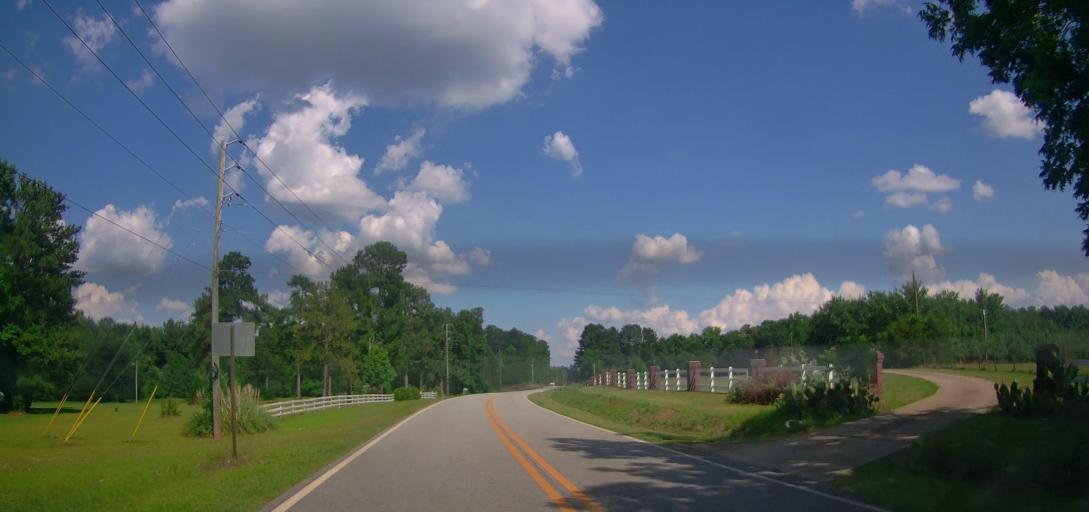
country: US
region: Georgia
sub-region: Henry County
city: Locust Grove
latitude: 33.2191
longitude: -84.0811
